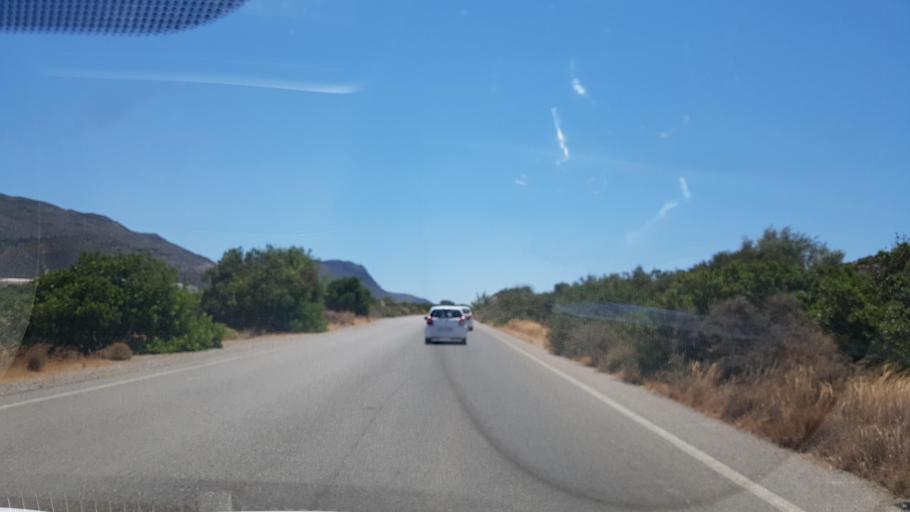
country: GR
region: Crete
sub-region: Nomos Chanias
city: Palaiochora
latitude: 35.2930
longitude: 23.5442
